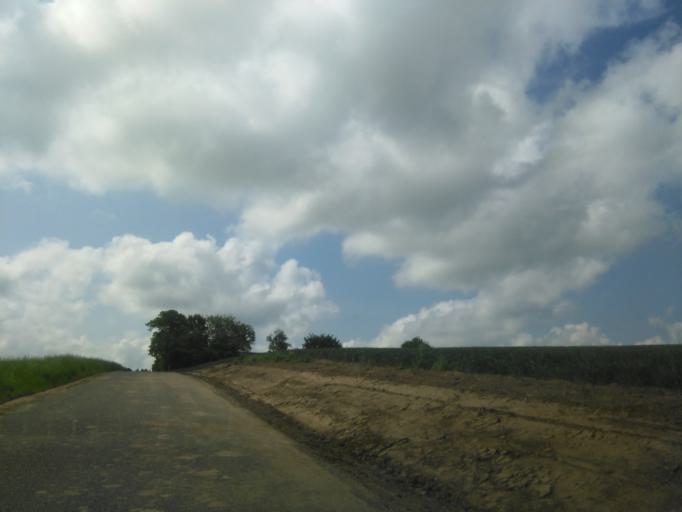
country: DK
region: Central Jutland
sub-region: Skanderborg Kommune
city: Skovby
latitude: 56.2052
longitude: 9.9690
